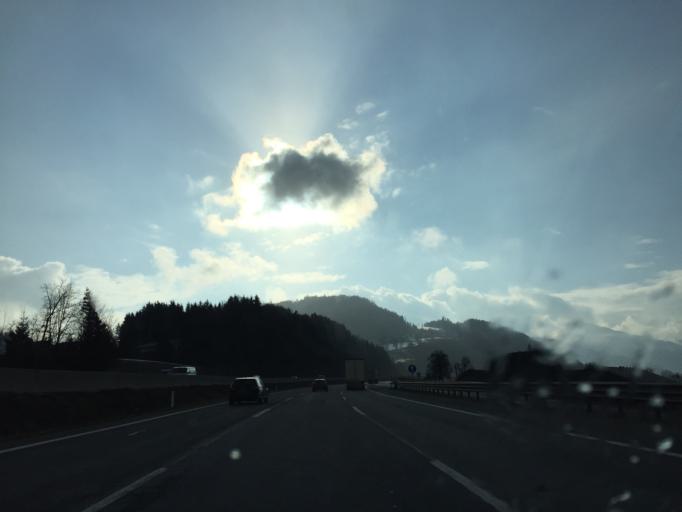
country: AT
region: Salzburg
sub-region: Politischer Bezirk Sankt Johann im Pongau
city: Pfarrwerfen
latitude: 47.4583
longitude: 13.2108
